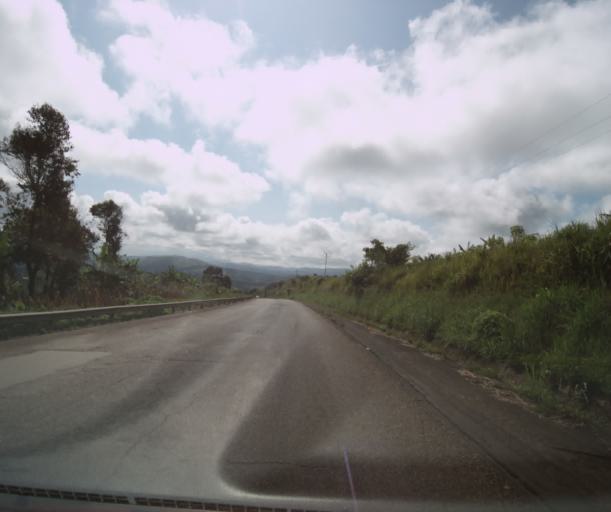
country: CM
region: West
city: Bafoussam
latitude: 5.4824
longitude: 10.4936
